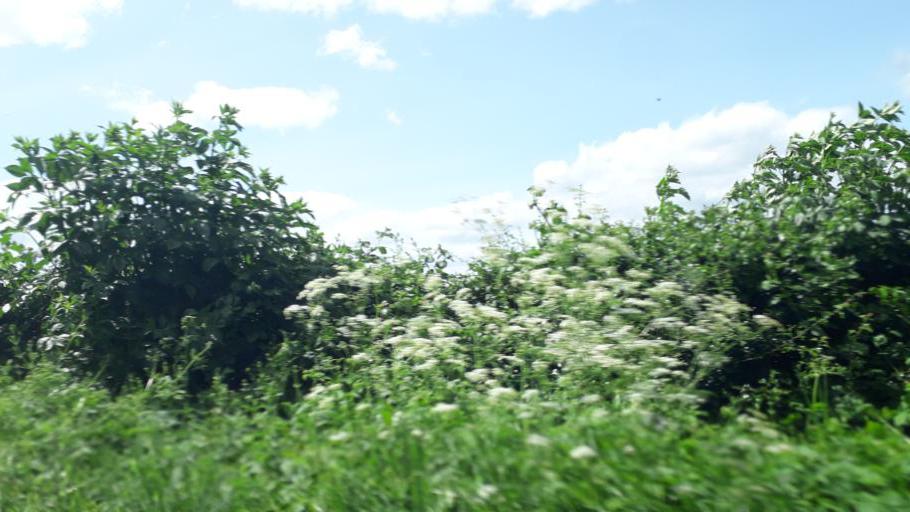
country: IE
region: Leinster
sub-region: Kildare
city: Moone
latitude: 53.0096
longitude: -6.8063
